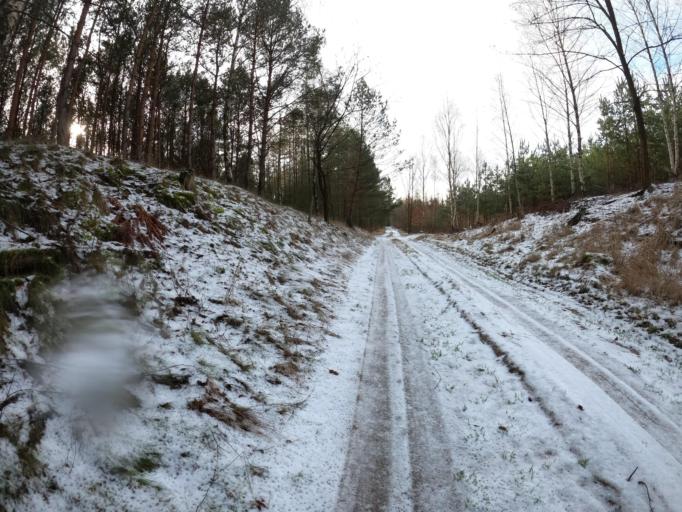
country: PL
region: Lubusz
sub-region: Powiat slubicki
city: Rzepin
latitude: 52.2832
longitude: 14.8038
